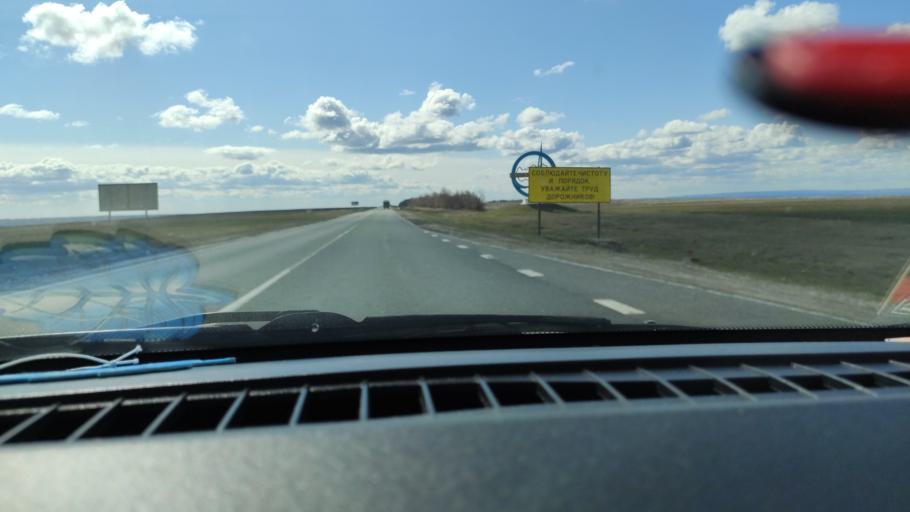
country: RU
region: Saratov
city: Dukhovnitskoye
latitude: 52.7984
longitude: 48.2307
